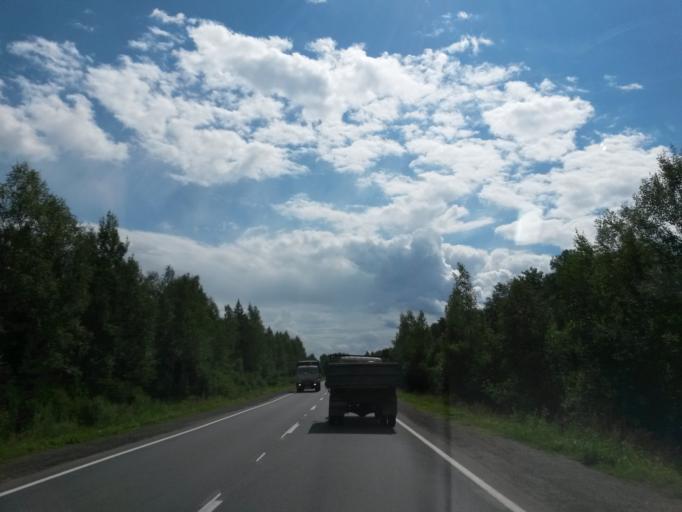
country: RU
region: Jaroslavl
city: Gavrilov-Yam
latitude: 57.2918
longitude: 39.9504
